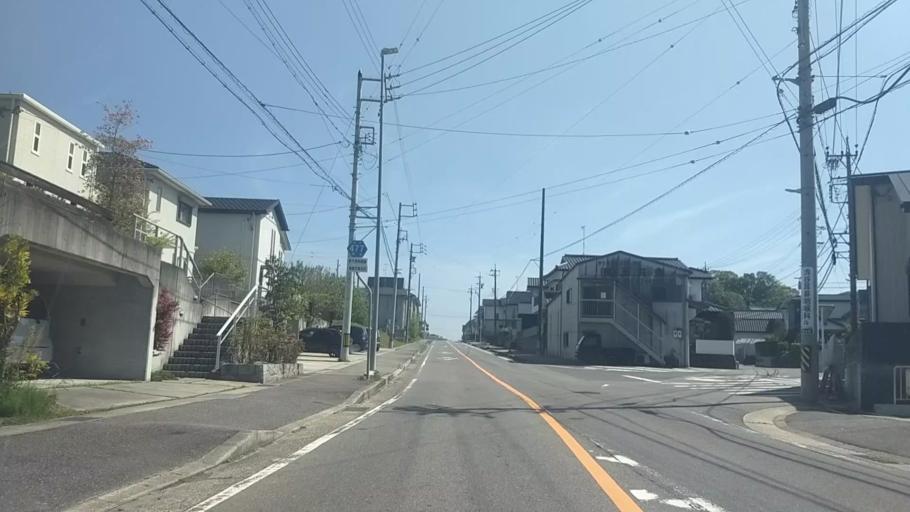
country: JP
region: Aichi
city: Okazaki
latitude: 34.9755
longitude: 137.1856
